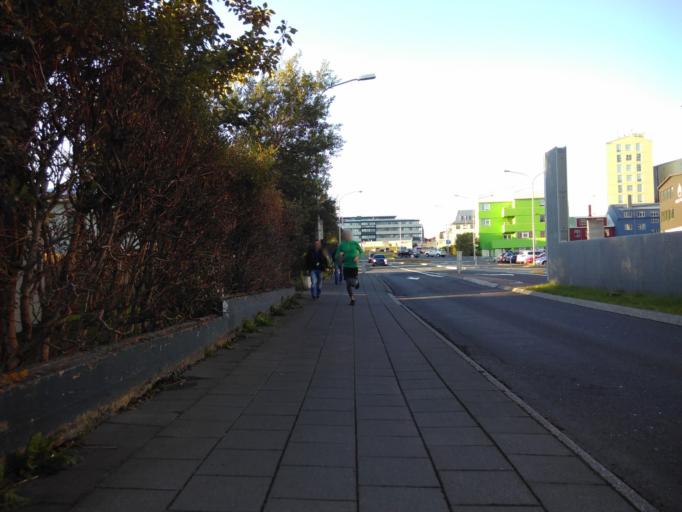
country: IS
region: Capital Region
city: Reykjavik
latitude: 64.1442
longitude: -21.9067
